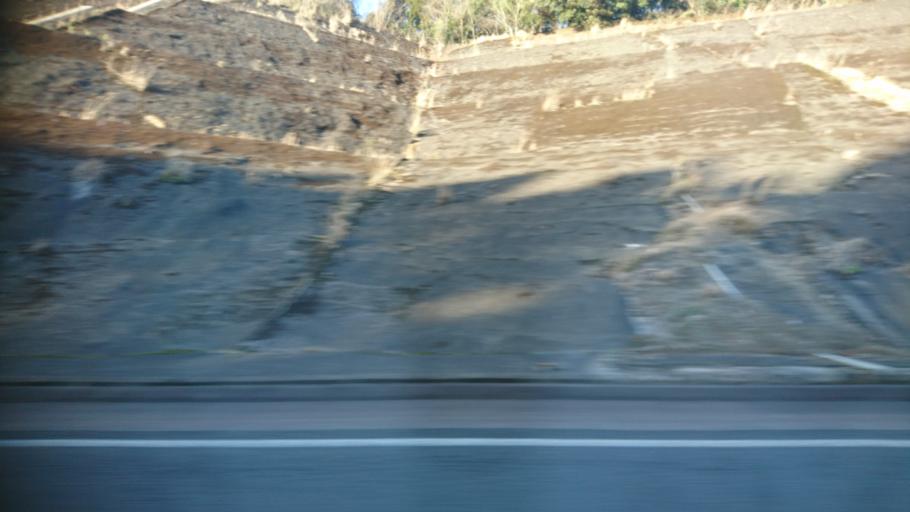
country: JP
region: Miyazaki
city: Miyakonojo
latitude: 31.7953
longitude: 131.1724
